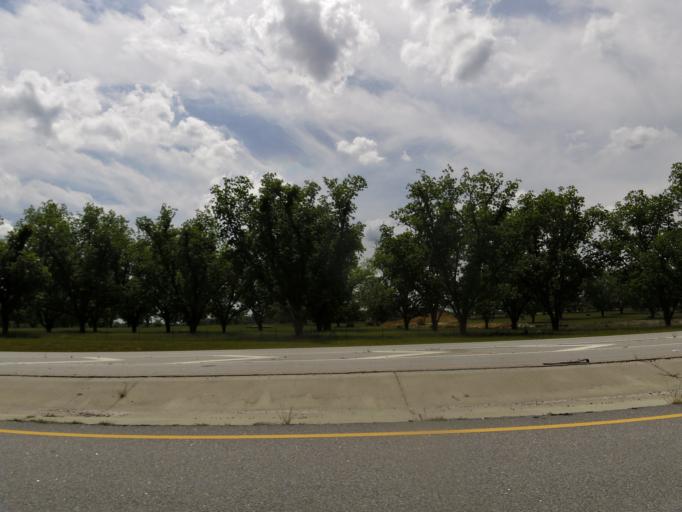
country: US
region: Georgia
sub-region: Jefferson County
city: Wadley
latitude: 32.7978
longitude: -82.3987
